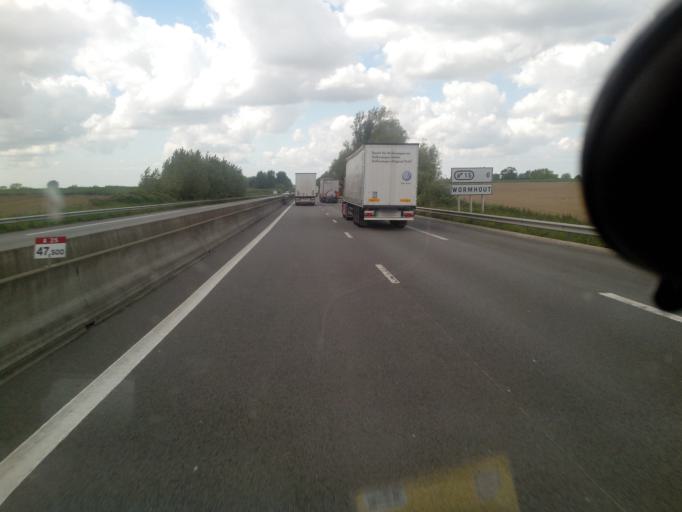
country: FR
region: Nord-Pas-de-Calais
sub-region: Departement du Nord
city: Winnezeele
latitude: 50.8420
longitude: 2.5673
